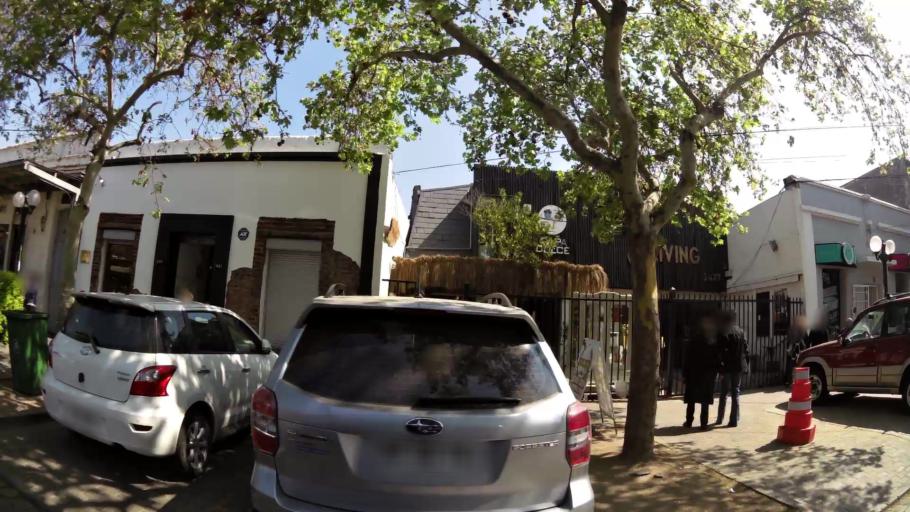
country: CL
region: Santiago Metropolitan
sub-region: Provincia de Santiago
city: Santiago
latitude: -33.4481
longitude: -70.6247
